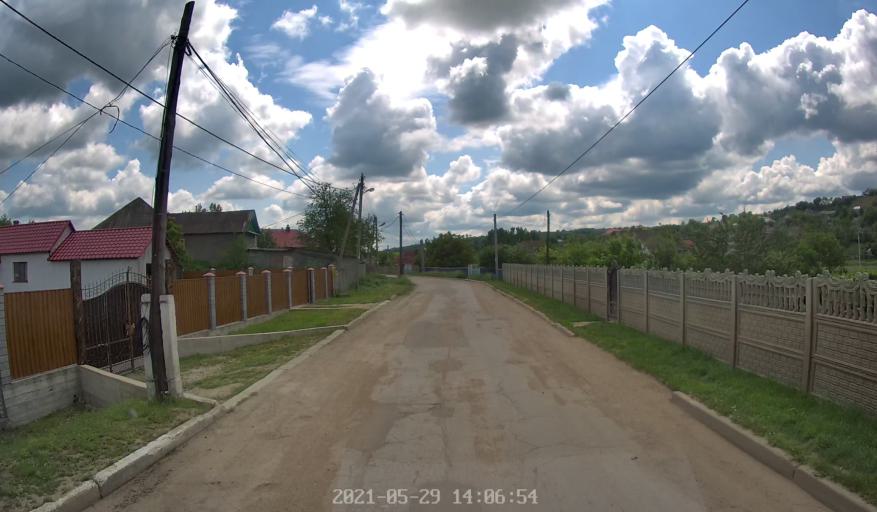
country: MD
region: Hincesti
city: Hincesti
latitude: 46.8332
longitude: 28.6760
